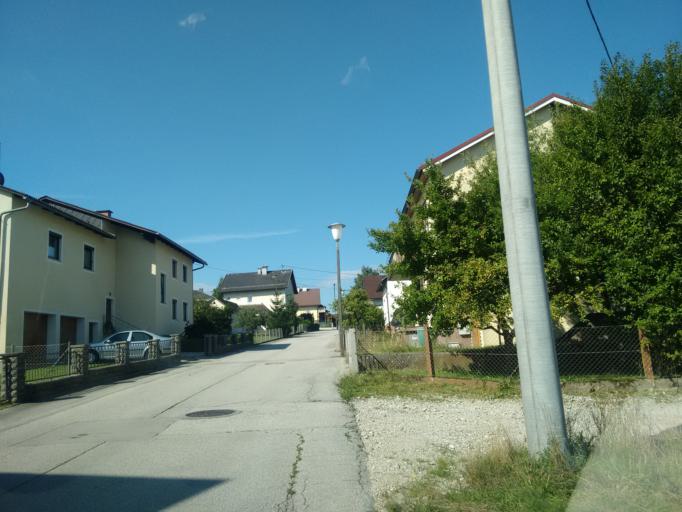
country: AT
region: Upper Austria
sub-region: Politischer Bezirk Steyr-Land
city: Bad Hall
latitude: 48.0266
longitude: 14.2199
